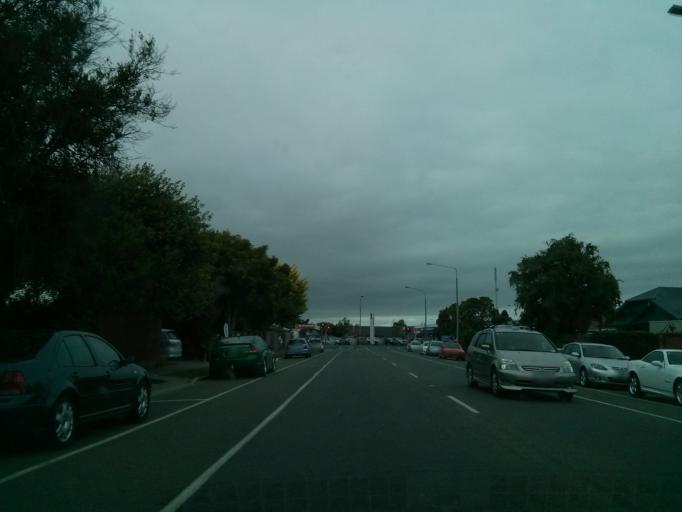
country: NZ
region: Canterbury
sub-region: Christchurch City
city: Christchurch
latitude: -43.5296
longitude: 172.5869
